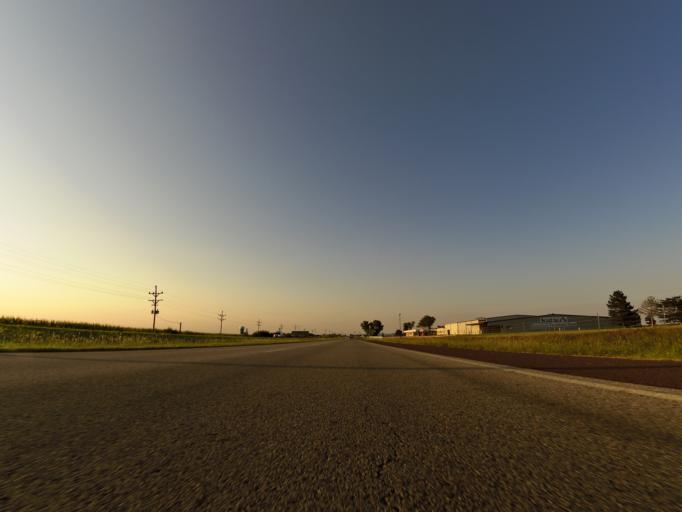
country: US
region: Kansas
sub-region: Reno County
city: South Hutchinson
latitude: 38.0002
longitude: -97.9404
